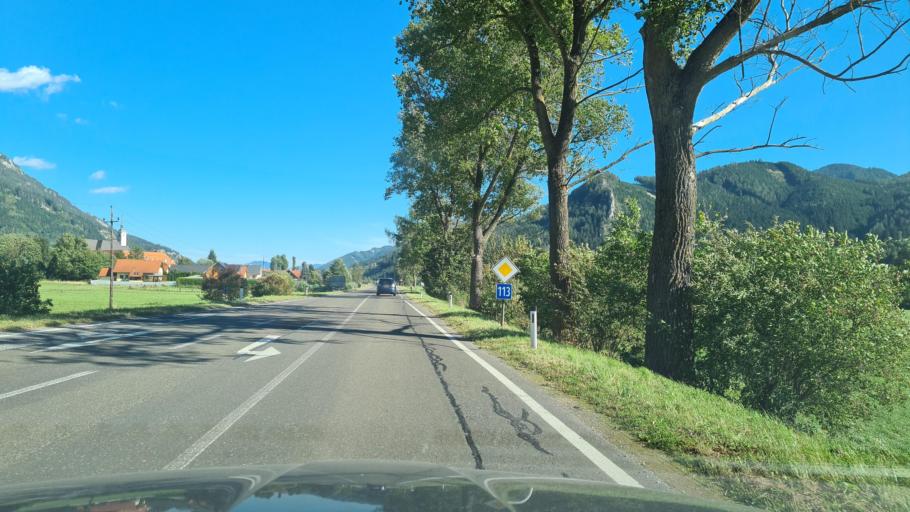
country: AT
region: Styria
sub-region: Politischer Bezirk Leoben
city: Mautern in Steiermark
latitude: 47.3991
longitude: 14.8160
